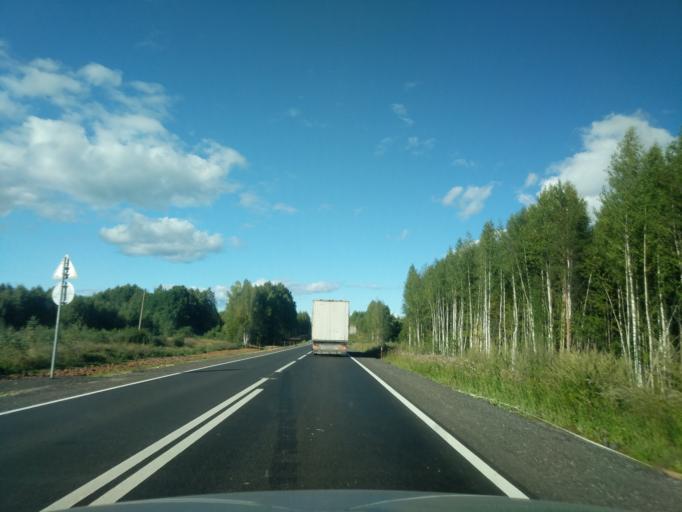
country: RU
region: Kostroma
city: Makar'yev
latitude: 57.9905
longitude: 43.9669
